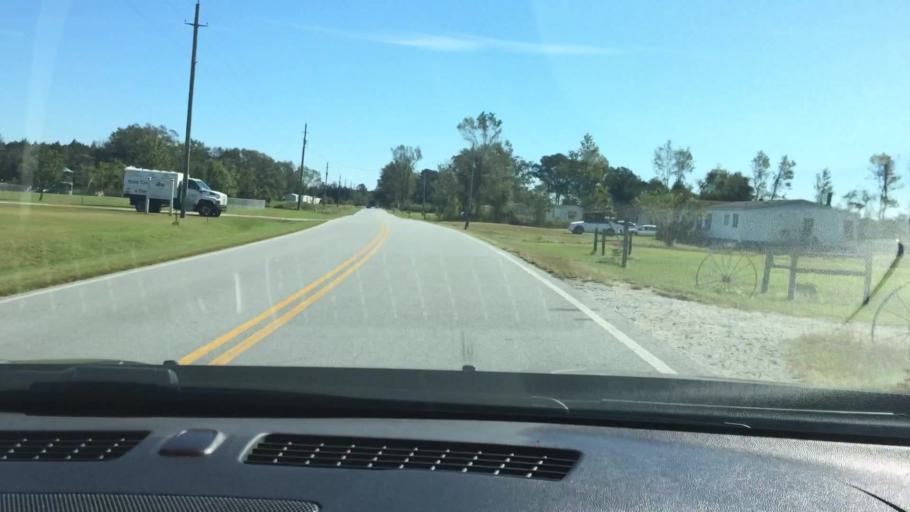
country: US
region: North Carolina
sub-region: Pitt County
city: Grifton
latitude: 35.3775
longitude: -77.3666
